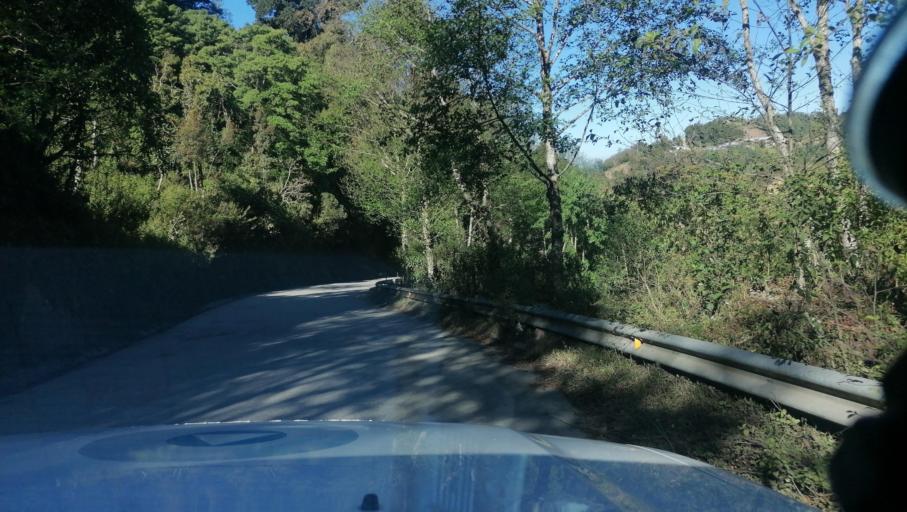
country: MX
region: Chiapas
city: Motozintla de Mendoza
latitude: 15.2652
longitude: -92.2190
